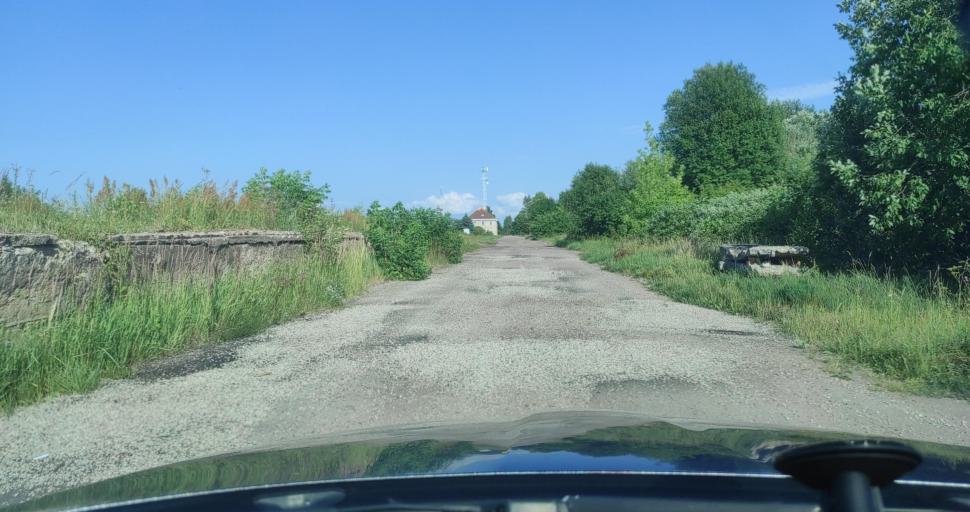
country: LV
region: Skrunda
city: Skrunda
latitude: 56.6806
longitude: 22.0071
